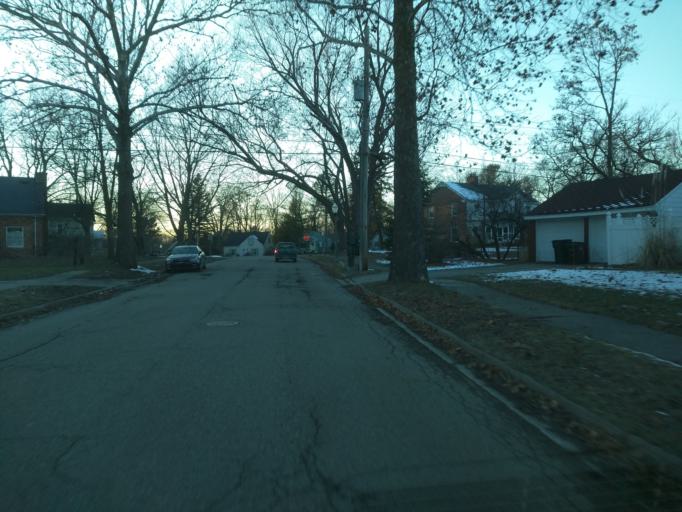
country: US
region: Michigan
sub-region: Ingham County
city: Lansing
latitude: 42.6985
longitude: -84.5419
